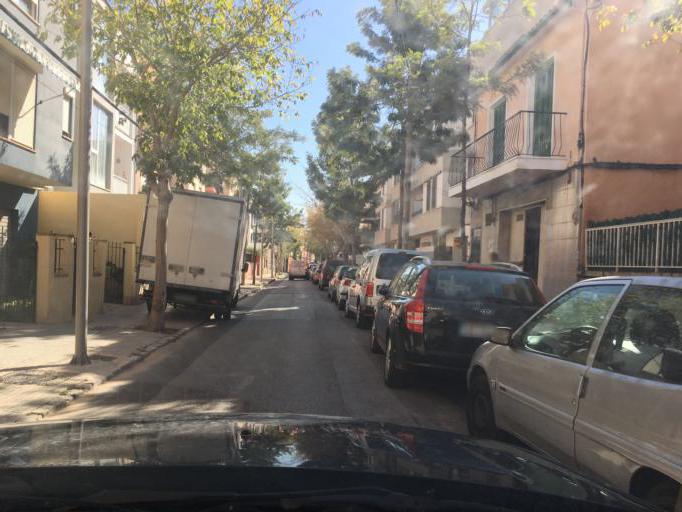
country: ES
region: Balearic Islands
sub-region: Illes Balears
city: Palma
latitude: 39.5847
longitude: 2.6754
